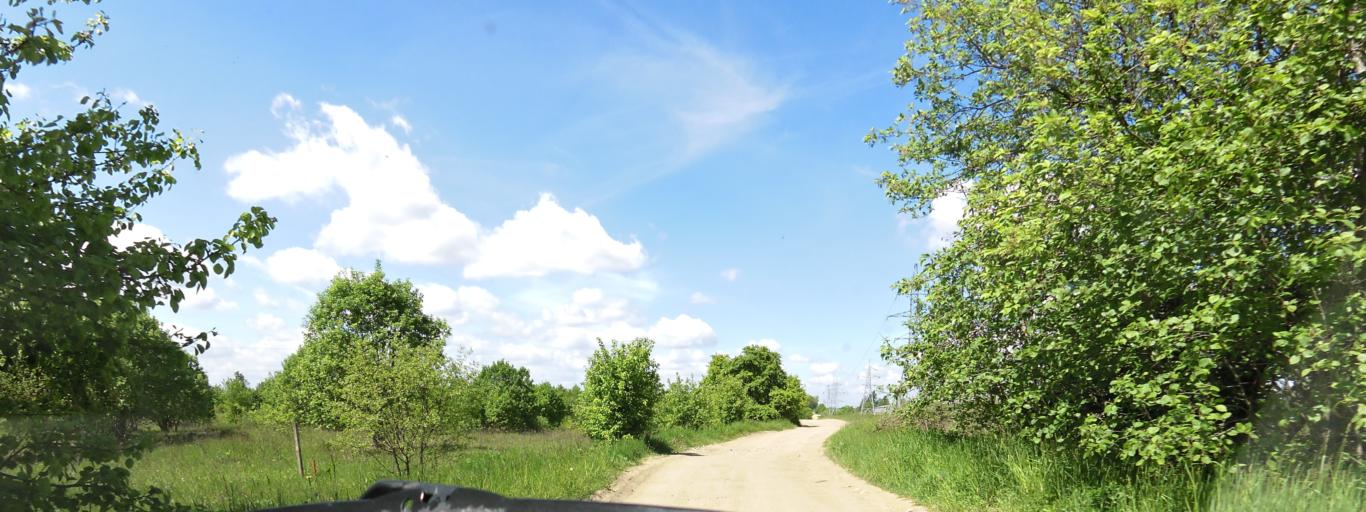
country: LT
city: Lentvaris
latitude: 54.6361
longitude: 25.0758
